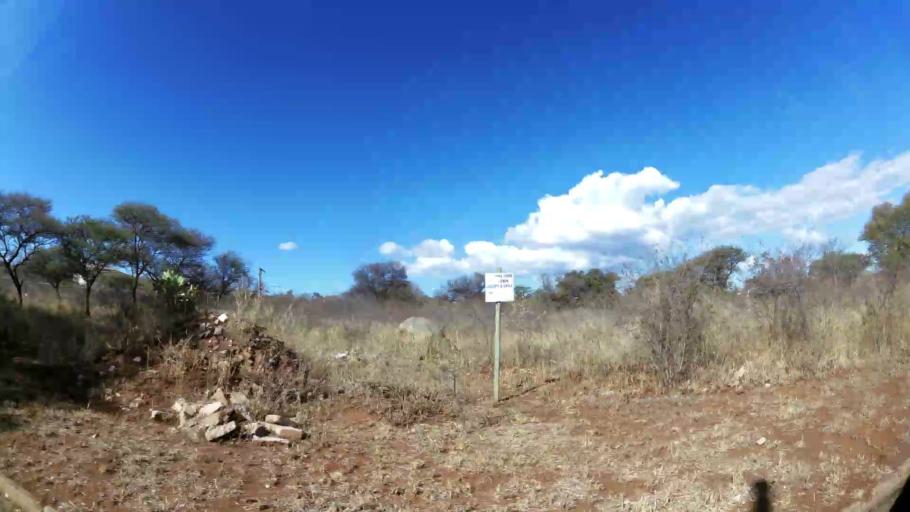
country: ZA
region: Limpopo
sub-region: Waterberg District Municipality
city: Mokopane
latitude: -24.1875
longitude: 29.0182
